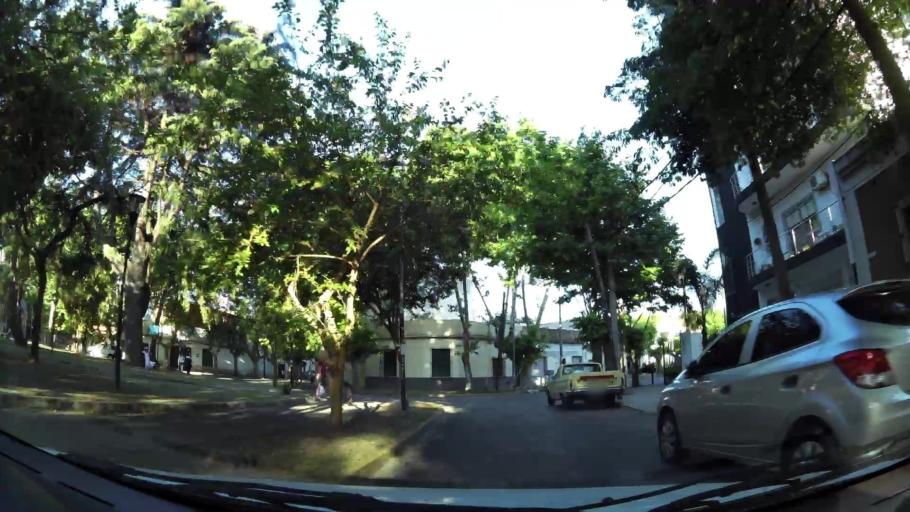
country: AR
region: Buenos Aires
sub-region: Partido de General San Martin
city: General San Martin
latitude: -34.5506
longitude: -58.5477
